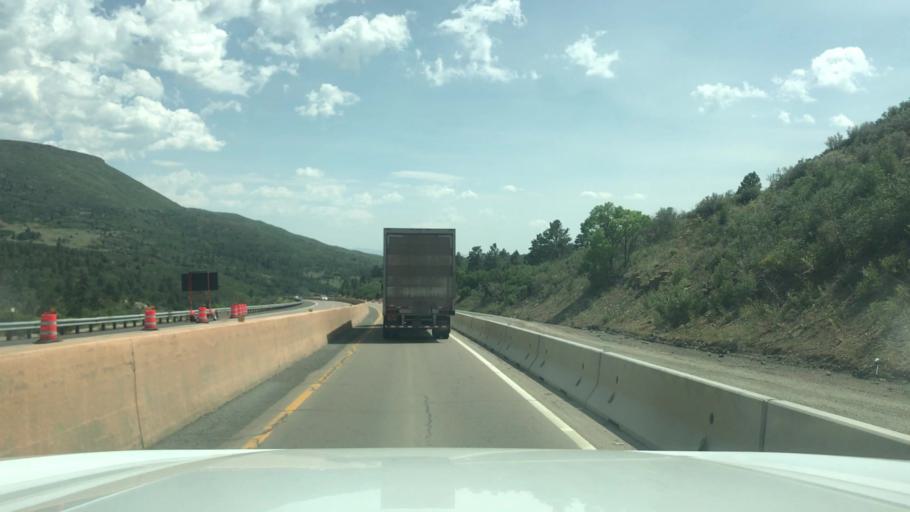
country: US
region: New Mexico
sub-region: Colfax County
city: Raton
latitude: 36.9808
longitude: -104.4826
